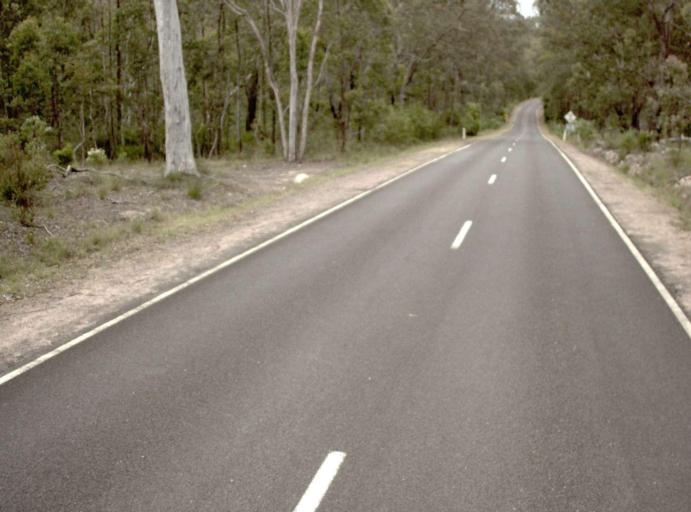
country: AU
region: Victoria
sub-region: East Gippsland
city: Bairnsdale
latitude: -37.6403
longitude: 147.2536
